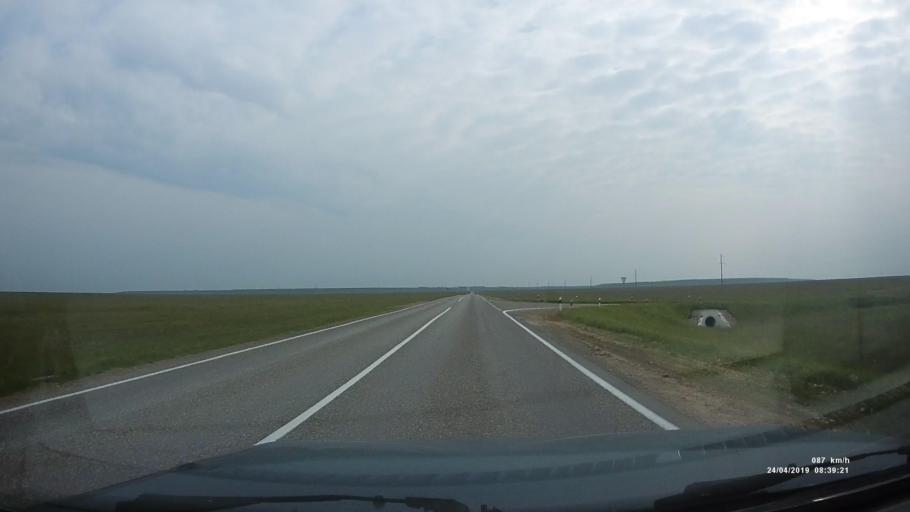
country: RU
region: Kalmykiya
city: Arshan'
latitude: 46.2204
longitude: 43.9825
